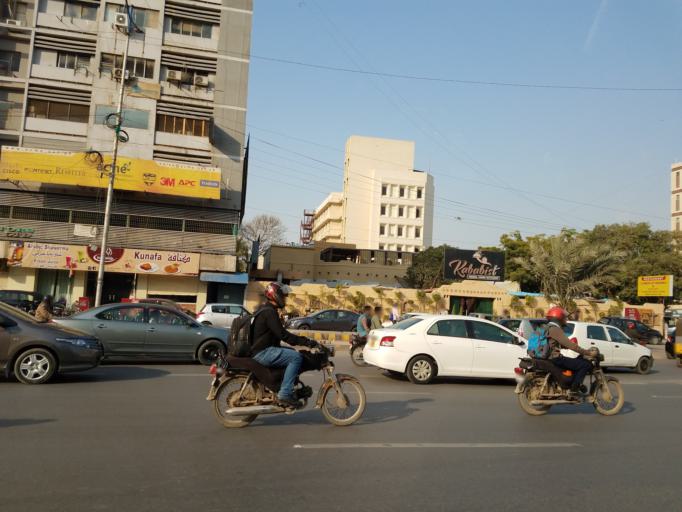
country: PK
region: Sindh
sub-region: Karachi District
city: Karachi
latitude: 24.8598
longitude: 67.0542
